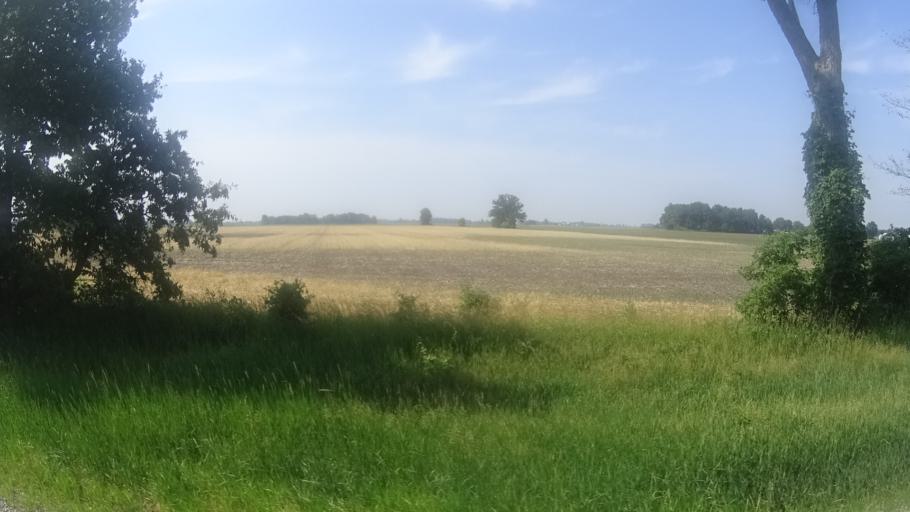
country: US
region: Ohio
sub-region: Huron County
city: Monroeville
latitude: 41.2880
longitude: -82.7414
